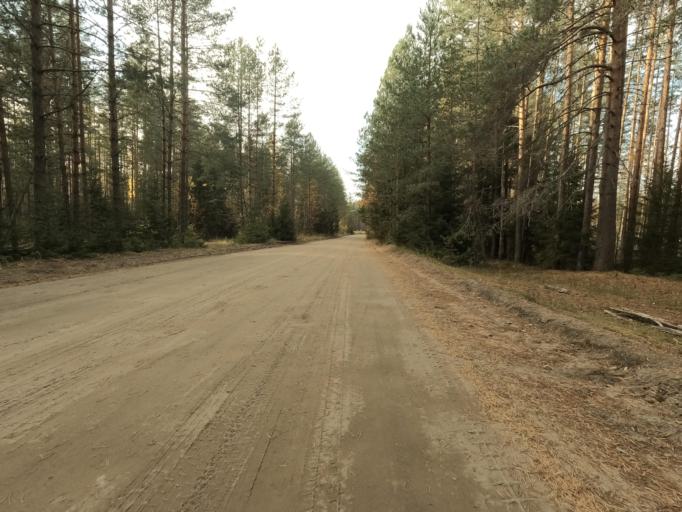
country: RU
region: Leningrad
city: Priladozhskiy
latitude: 59.6309
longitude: 31.3927
